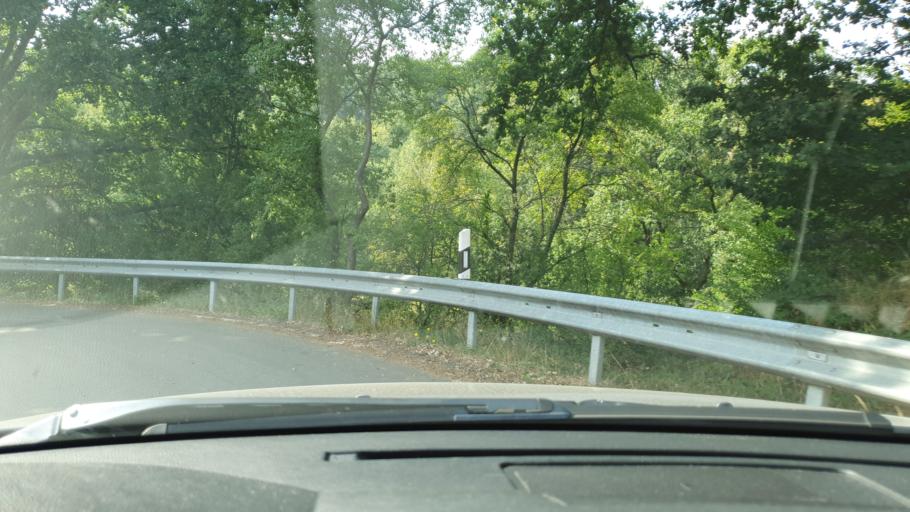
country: DE
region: Rheinland-Pfalz
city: Hettenhausen
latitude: 49.3405
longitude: 7.5521
